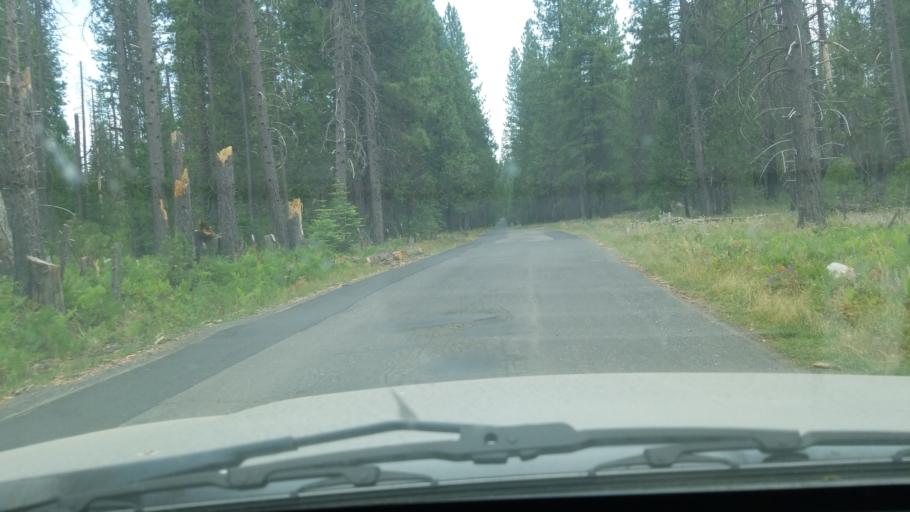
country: US
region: California
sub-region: Mariposa County
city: Yosemite Valley
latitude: 37.8351
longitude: -119.8472
